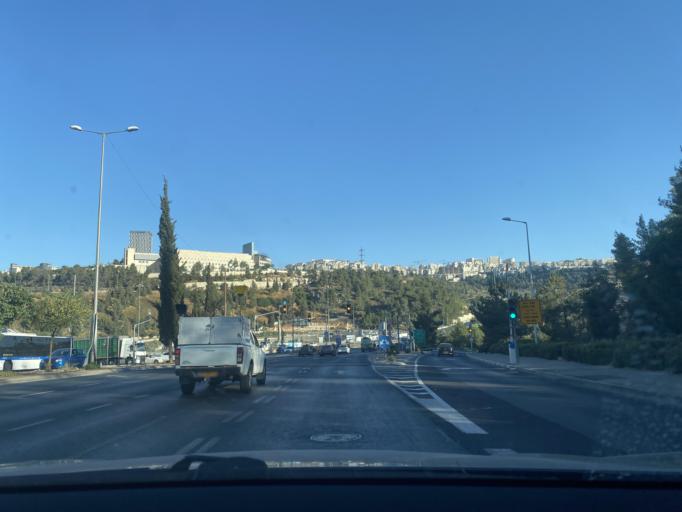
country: PS
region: West Bank
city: Bayt Iksa
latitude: 31.8097
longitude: 35.2037
